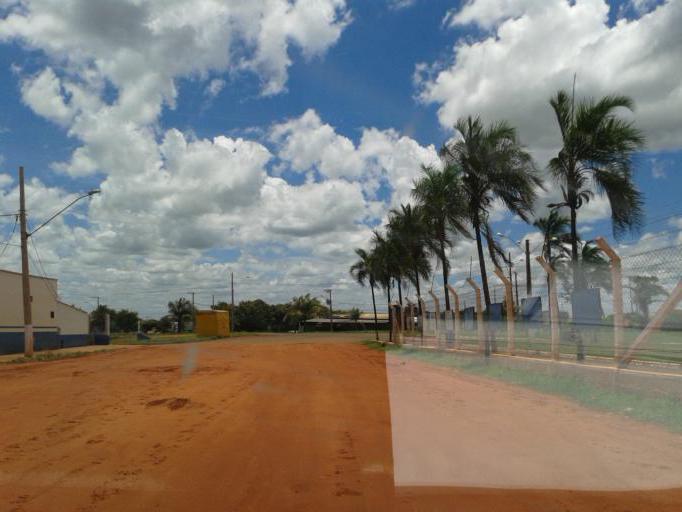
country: BR
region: Minas Gerais
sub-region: Santa Vitoria
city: Santa Vitoria
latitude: -18.8548
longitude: -50.1310
